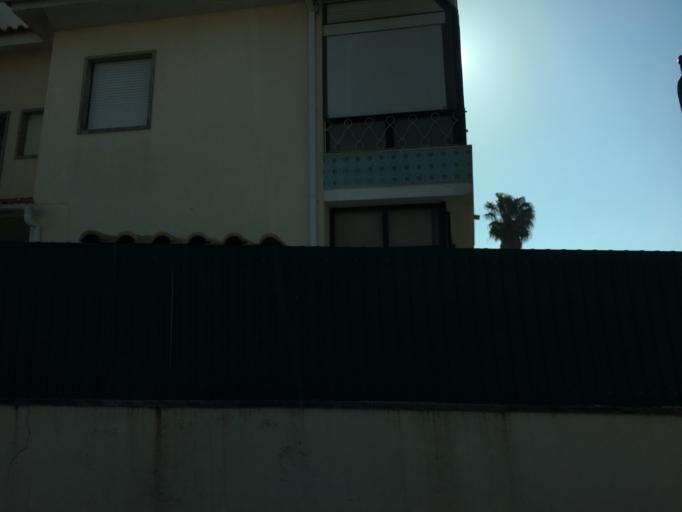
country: PT
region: Lisbon
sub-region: Cascais
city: Sao Domingos de Rana
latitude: 38.7132
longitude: -9.3445
